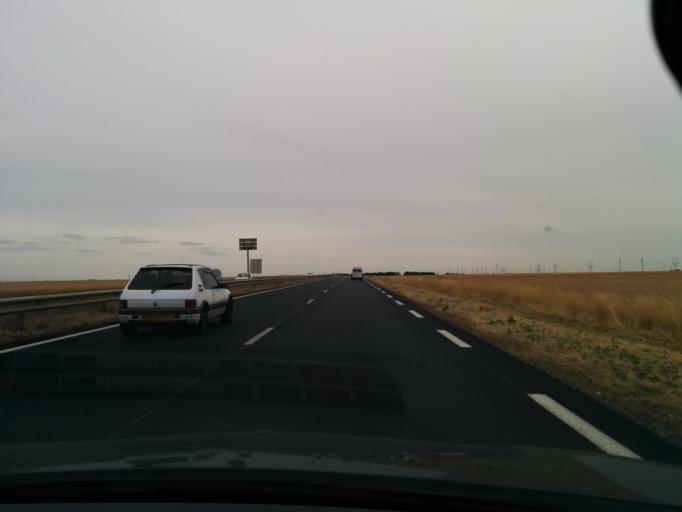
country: FR
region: Ile-de-France
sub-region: Departement de l'Essonne
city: Angerville
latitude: 48.2956
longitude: 1.9869
